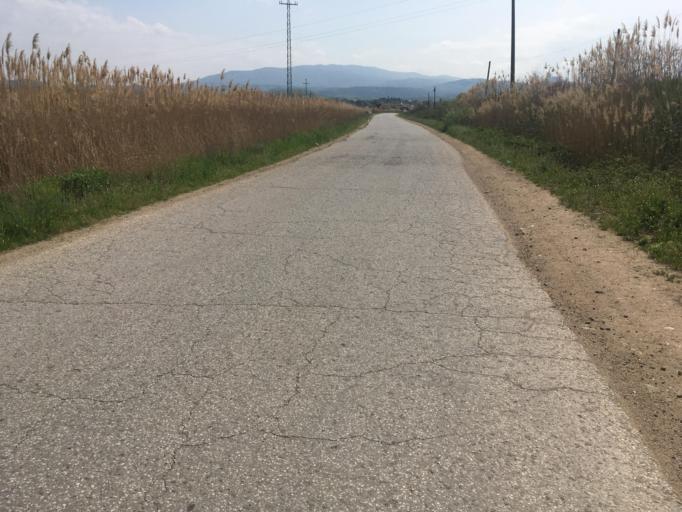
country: MK
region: Karbinci
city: Karbinci
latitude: 41.8010
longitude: 22.2113
